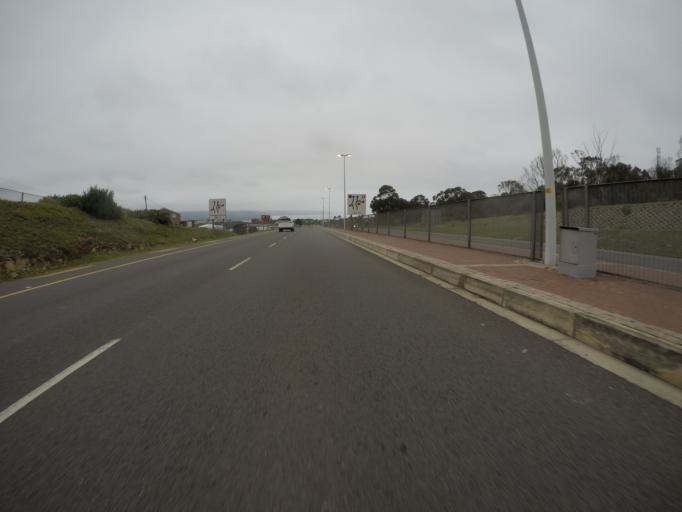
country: ZA
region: Western Cape
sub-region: Eden District Municipality
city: Plettenberg Bay
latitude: -34.0510
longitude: 23.3543
